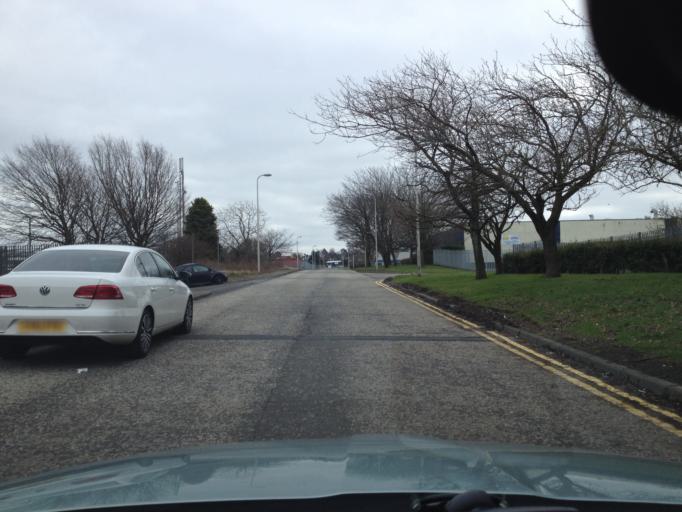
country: GB
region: Scotland
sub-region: West Lothian
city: Livingston
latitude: 55.9084
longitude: -3.5017
